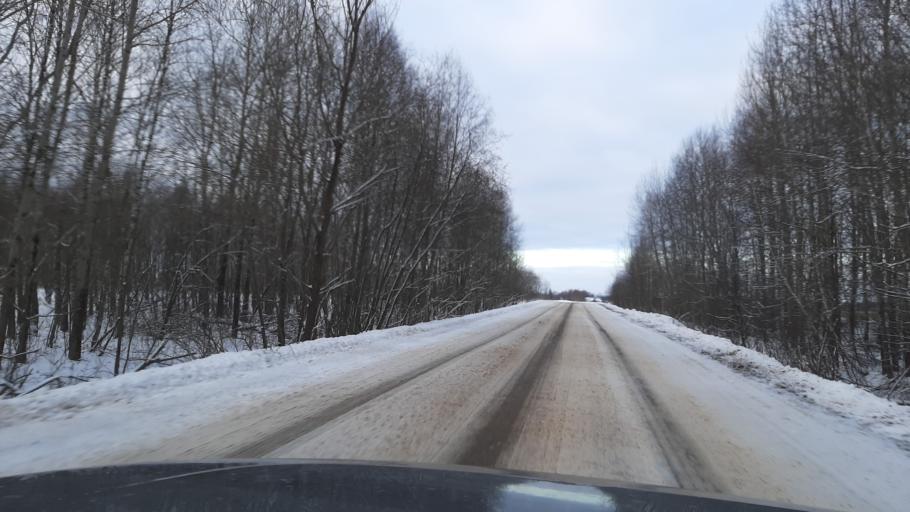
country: RU
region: Kostroma
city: Kosmynino
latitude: 57.4807
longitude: 40.7486
